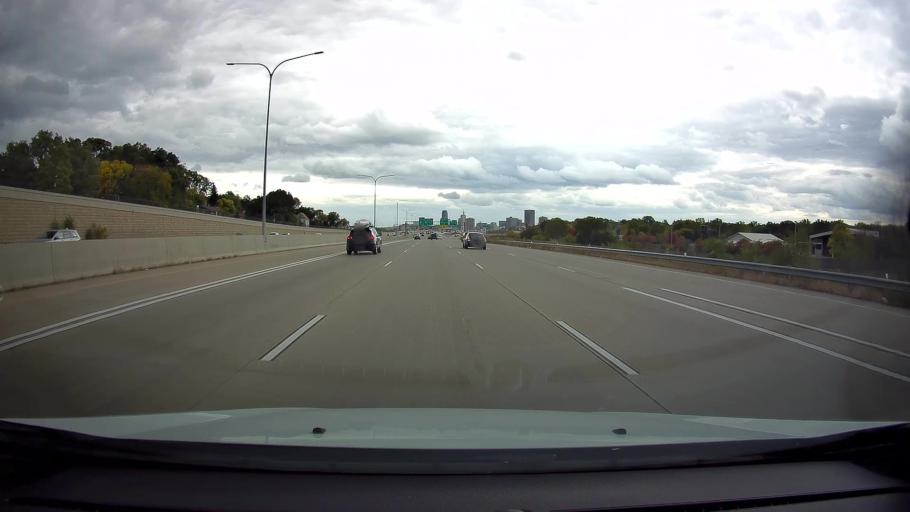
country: US
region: Minnesota
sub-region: Ramsey County
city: Saint Paul
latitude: 44.9738
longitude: -93.0889
